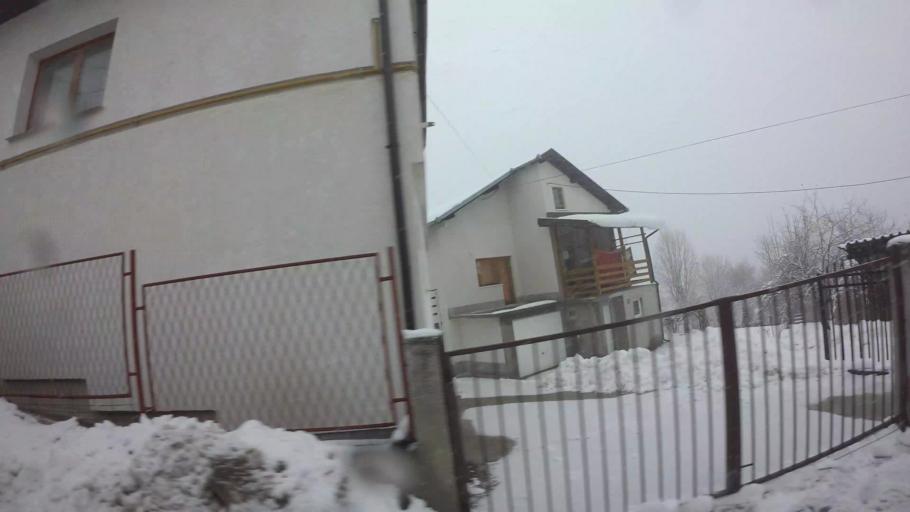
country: BA
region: Federation of Bosnia and Herzegovina
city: Kobilja Glava
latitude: 43.8520
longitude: 18.4441
